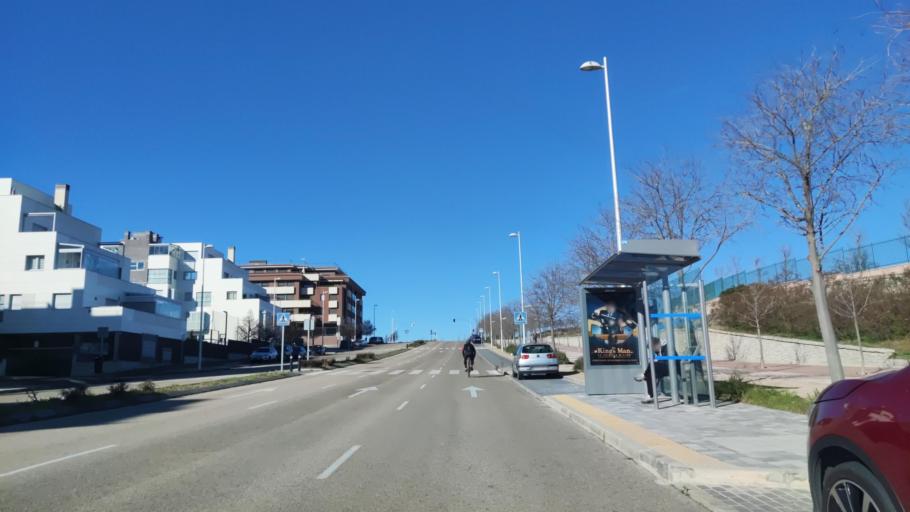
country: ES
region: Madrid
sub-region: Provincia de Madrid
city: Hortaleza
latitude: 40.4855
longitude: -3.6311
